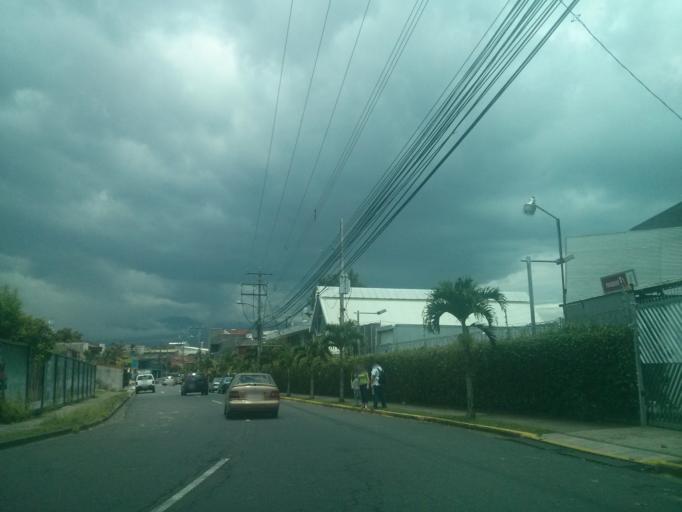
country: CR
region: San Jose
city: San Pedro
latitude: 9.9256
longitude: -84.0653
